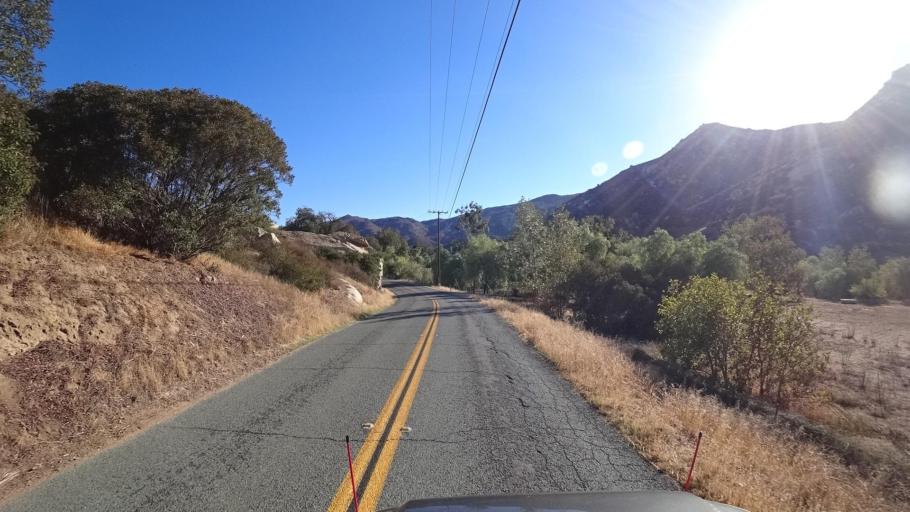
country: MX
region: Baja California
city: Tecate
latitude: 32.6241
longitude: -116.6902
